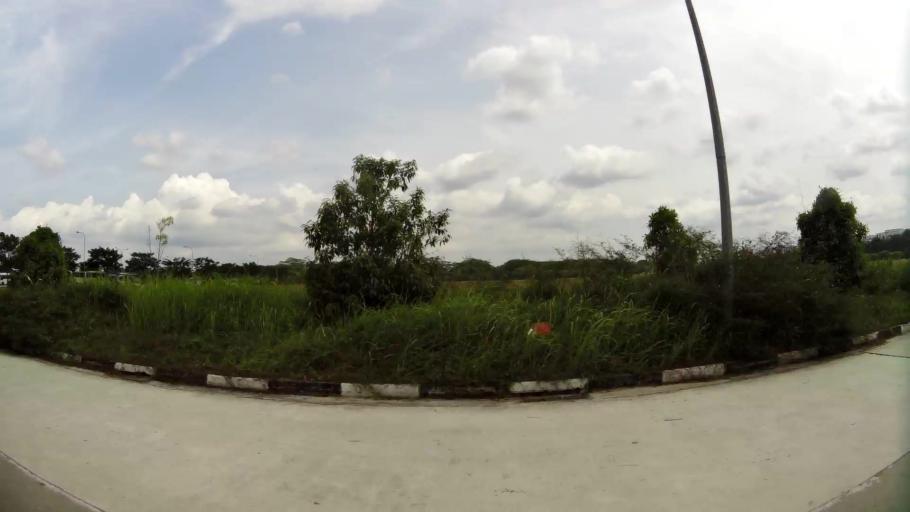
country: MY
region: Johor
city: Johor Bahru
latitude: 1.3550
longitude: 103.7098
